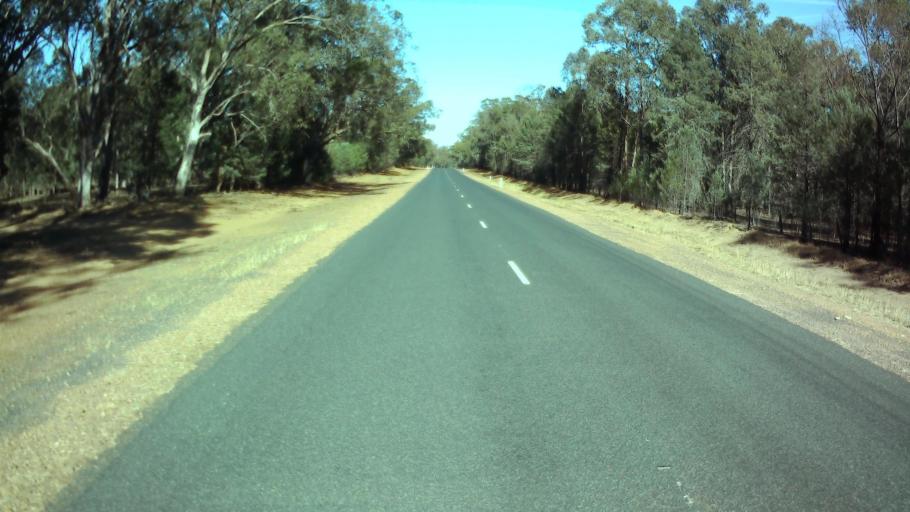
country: AU
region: New South Wales
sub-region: Weddin
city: Grenfell
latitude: -34.0273
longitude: 148.0562
